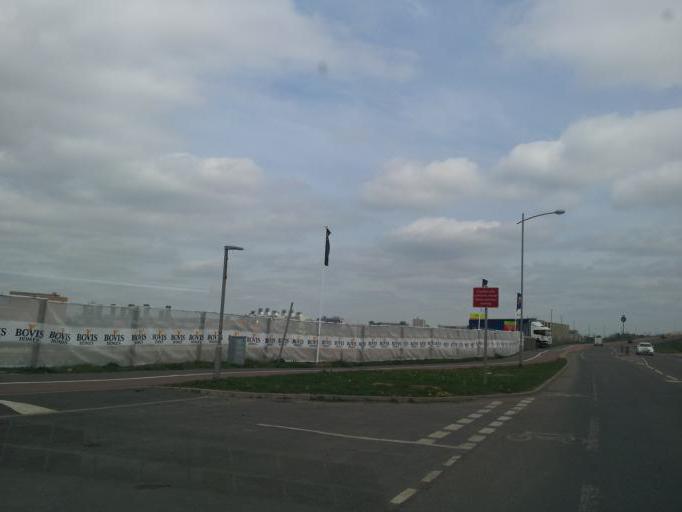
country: GB
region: England
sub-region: Cambridgeshire
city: Cambridge
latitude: 52.1670
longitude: 0.1257
